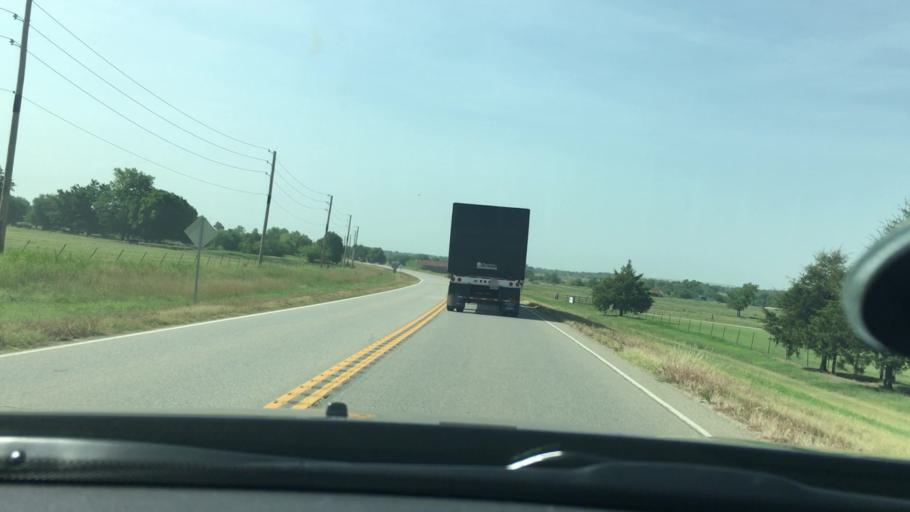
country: US
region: Oklahoma
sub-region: Coal County
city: Coalgate
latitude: 34.4647
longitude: -96.2171
